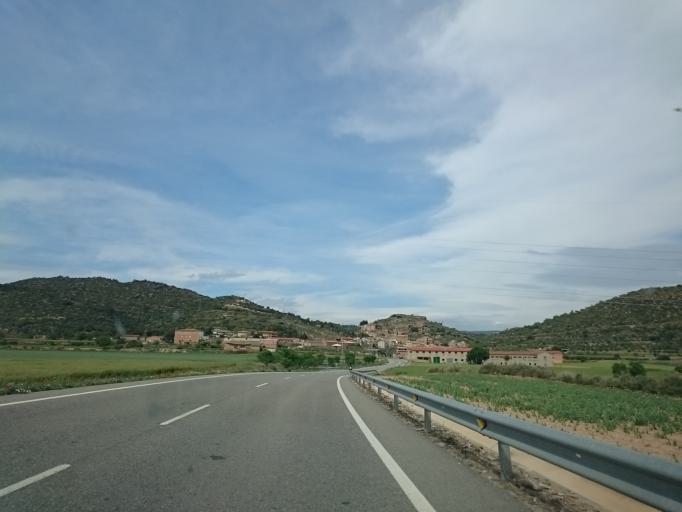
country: ES
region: Catalonia
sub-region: Provincia de Lleida
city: Tora de Riubregos
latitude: 41.8354
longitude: 1.3529
